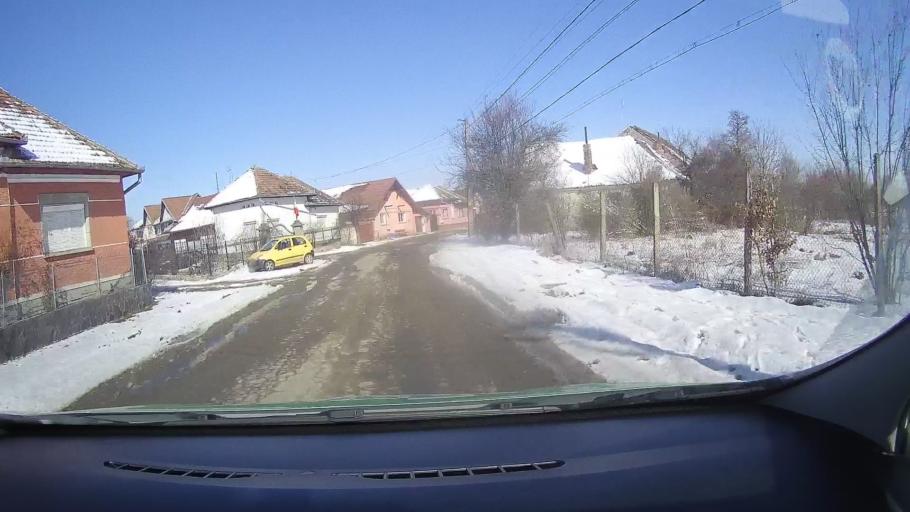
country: RO
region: Brasov
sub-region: Comuna Mandra
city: Mandra
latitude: 45.8248
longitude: 25.0088
